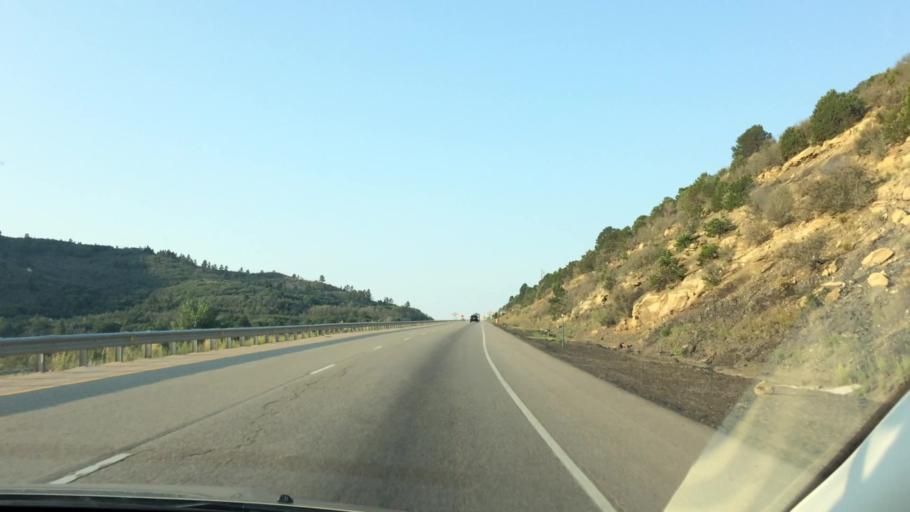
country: US
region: New Mexico
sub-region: Colfax County
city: Raton
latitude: 37.0069
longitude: -104.4805
